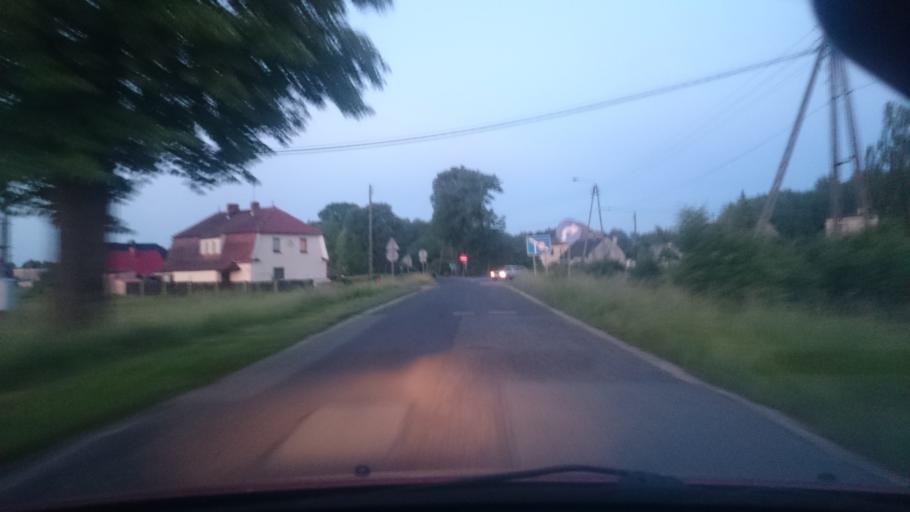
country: PL
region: Opole Voivodeship
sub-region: Powiat opolski
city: Ozimek
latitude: 50.6667
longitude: 18.1935
